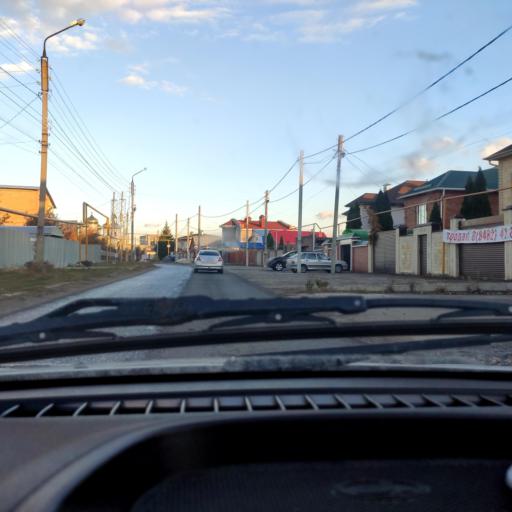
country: RU
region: Samara
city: Zhigulevsk
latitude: 53.4642
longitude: 49.6267
